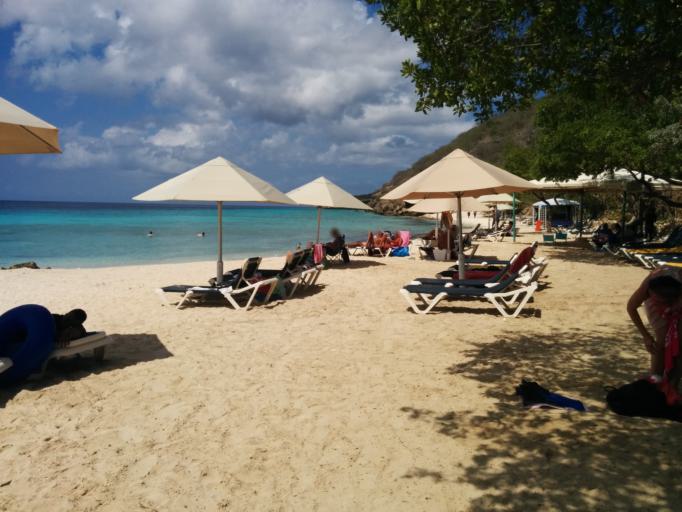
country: CW
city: Dorp Soto
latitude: 12.2191
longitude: -69.0860
